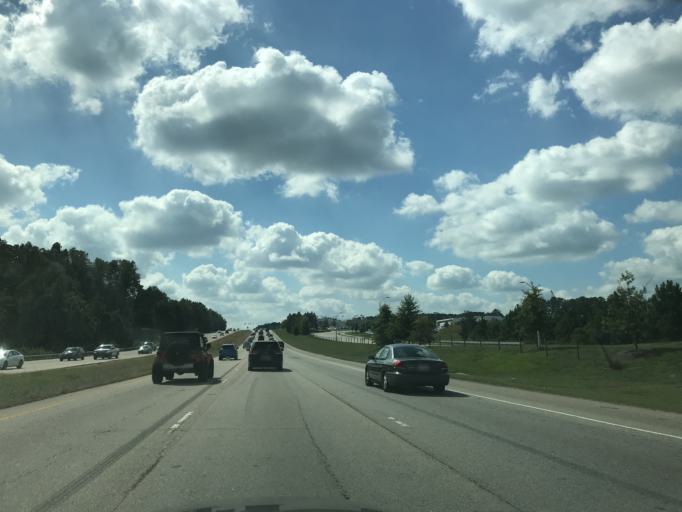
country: US
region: North Carolina
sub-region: Wake County
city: Wake Forest
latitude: 35.8893
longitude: -78.5634
